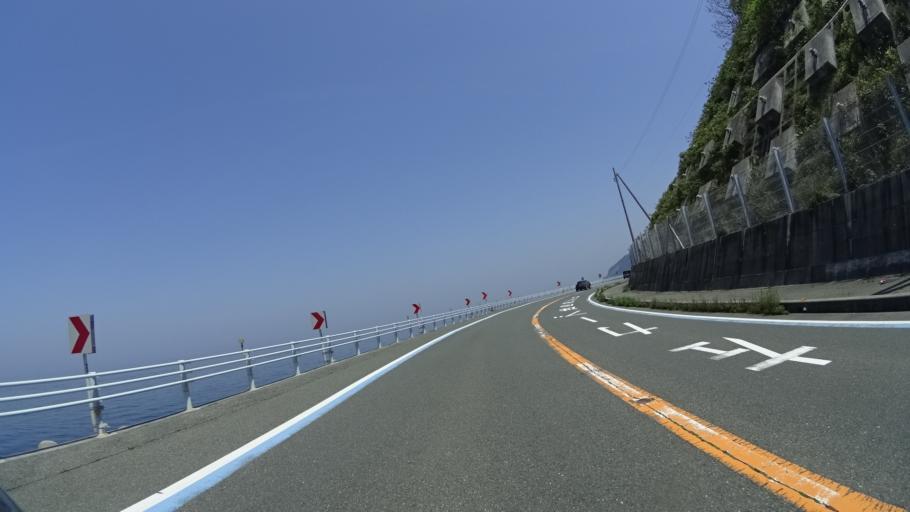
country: JP
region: Ehime
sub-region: Nishiuwa-gun
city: Ikata-cho
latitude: 33.5758
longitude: 132.4418
